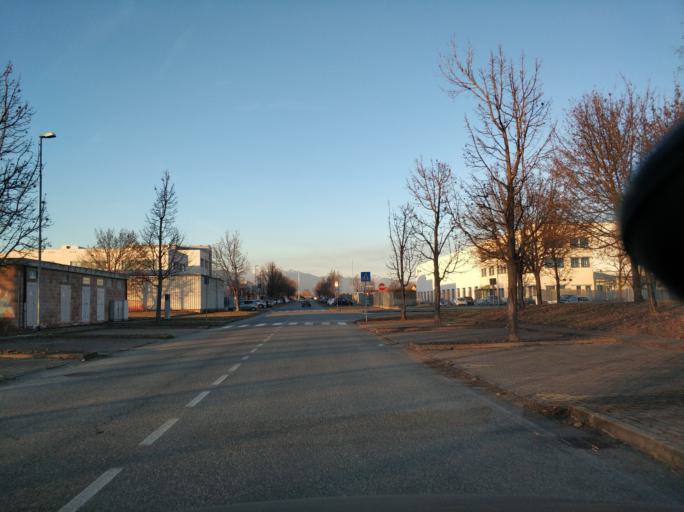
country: IT
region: Piedmont
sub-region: Provincia di Torino
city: San Maurizio
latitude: 45.2046
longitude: 7.6406
